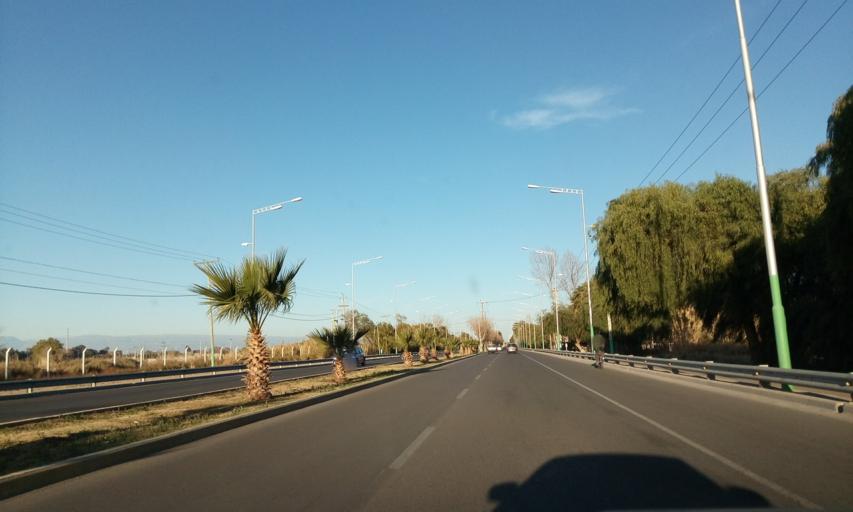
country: AR
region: San Juan
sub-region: Departamento de Rivadavia
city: Rivadavia
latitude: -31.5253
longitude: -68.6126
